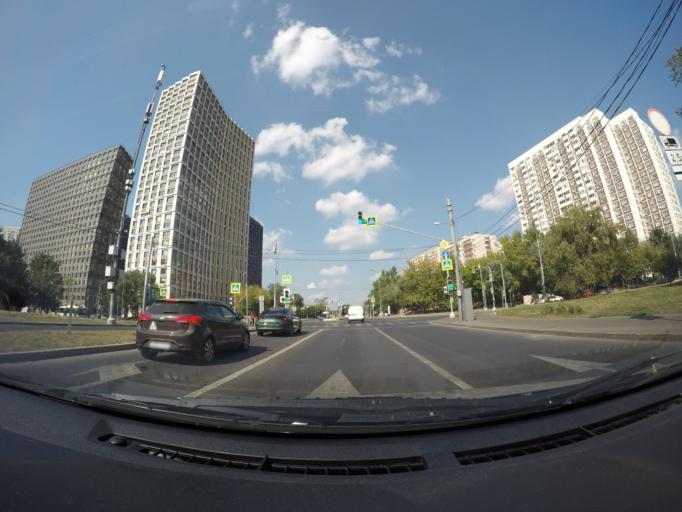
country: RU
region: Moscow
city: Novokhovrino
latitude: 55.8666
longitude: 37.4849
